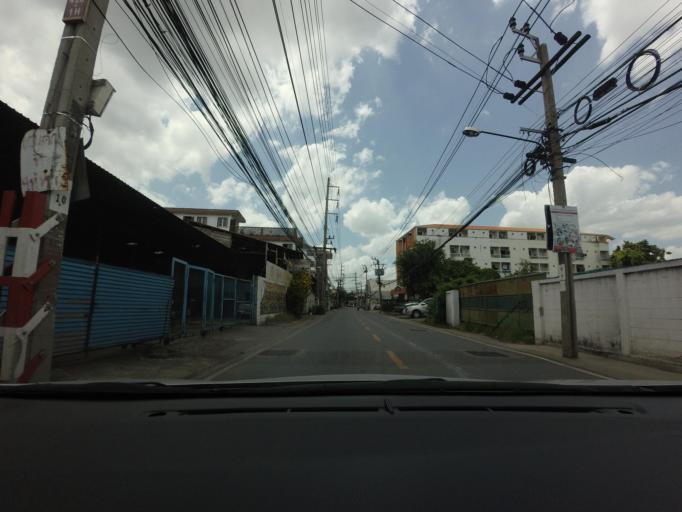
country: TH
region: Samut Prakan
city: Phra Samut Chedi
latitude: 13.6444
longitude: 100.5789
